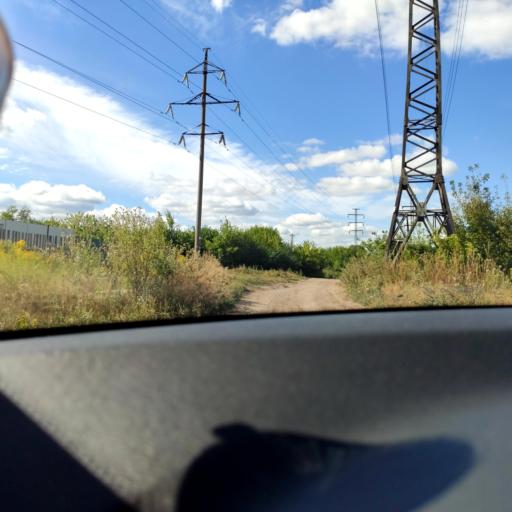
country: RU
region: Samara
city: Petra-Dubrava
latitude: 53.2913
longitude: 50.3074
